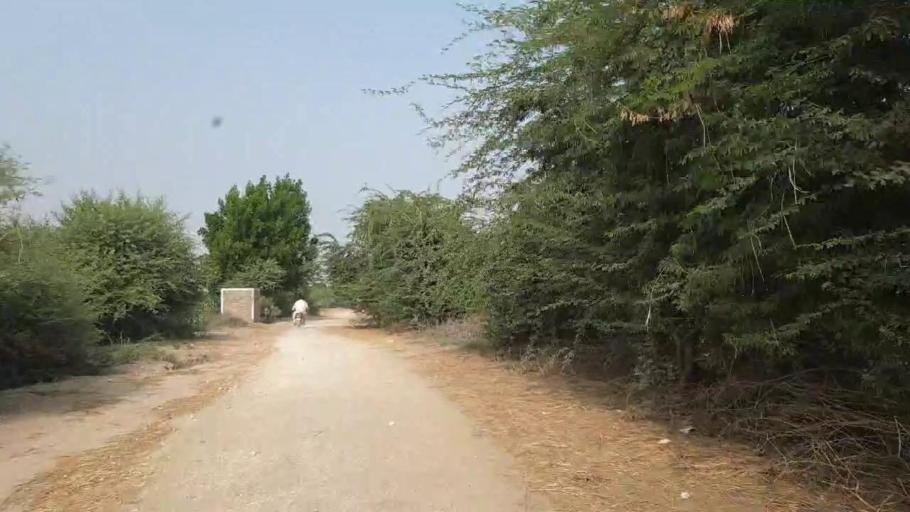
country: PK
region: Sindh
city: Kario
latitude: 24.9262
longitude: 68.6010
